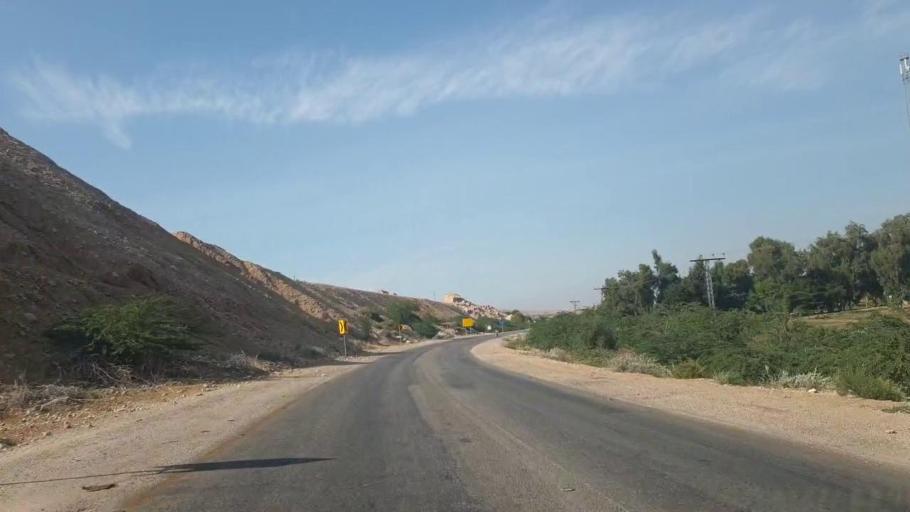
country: PK
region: Sindh
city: Sehwan
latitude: 26.3232
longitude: 67.8846
